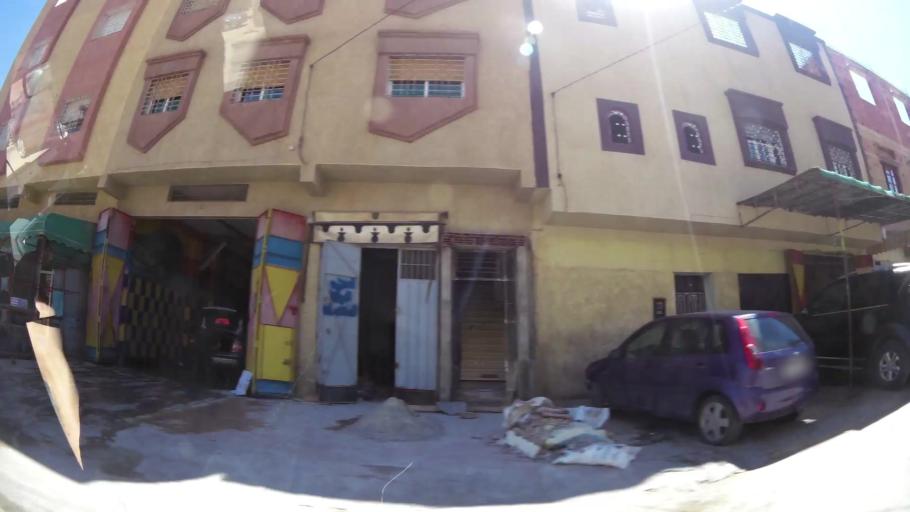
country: MA
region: Oriental
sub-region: Oujda-Angad
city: Oujda
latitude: 34.6653
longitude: -1.8818
